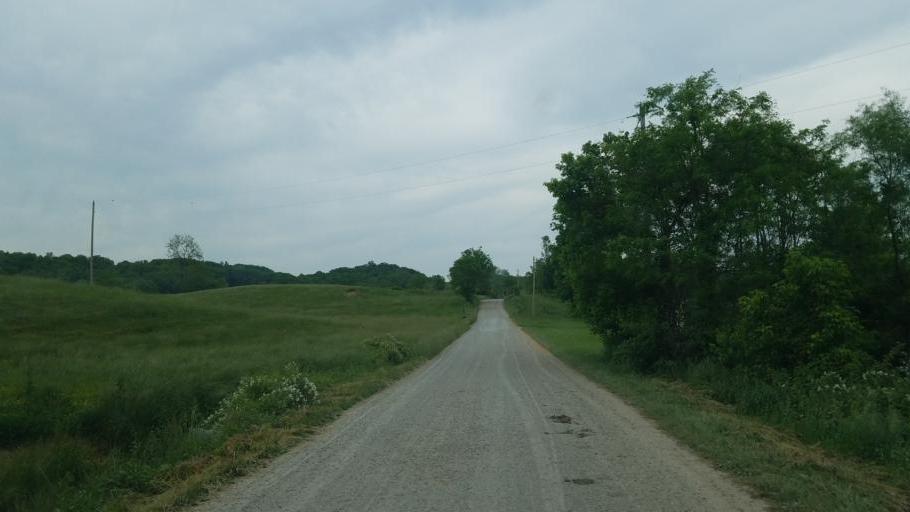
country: US
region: Ohio
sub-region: Meigs County
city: Pomeroy
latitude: 39.1198
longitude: -82.1498
